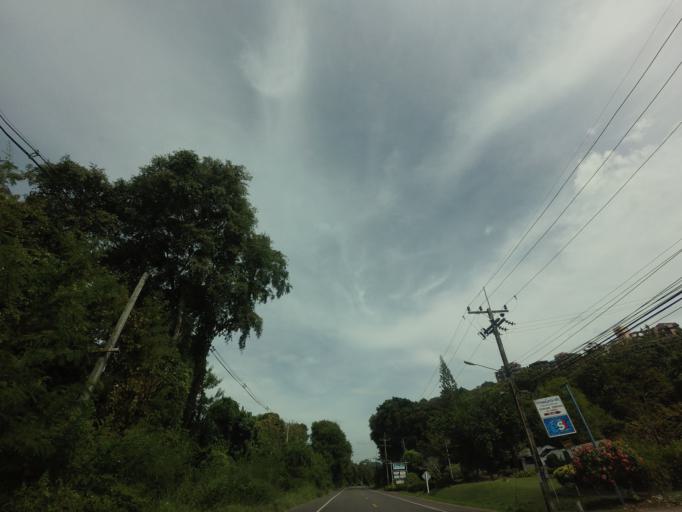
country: TH
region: Rayong
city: Klaeng
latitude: 12.6390
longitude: 101.5597
